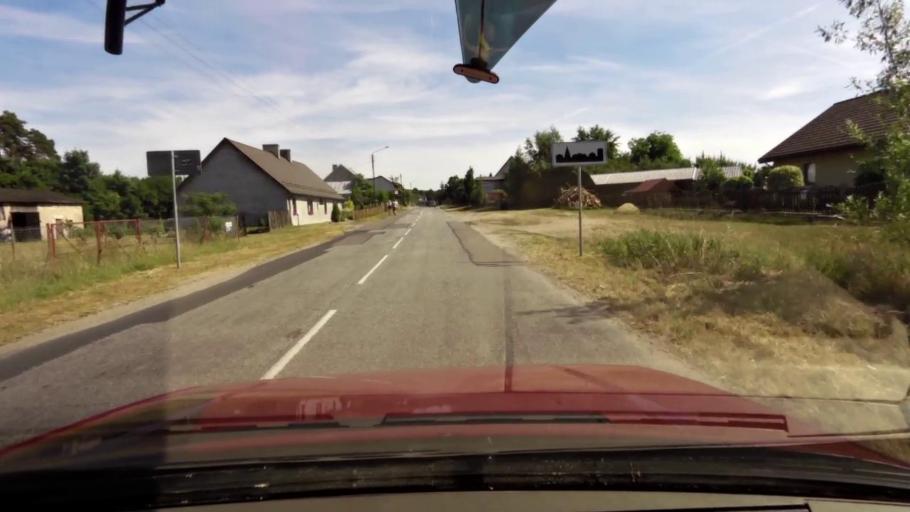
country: PL
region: Pomeranian Voivodeship
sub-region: Powiat slupski
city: Kepice
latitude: 54.2798
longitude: 16.9587
